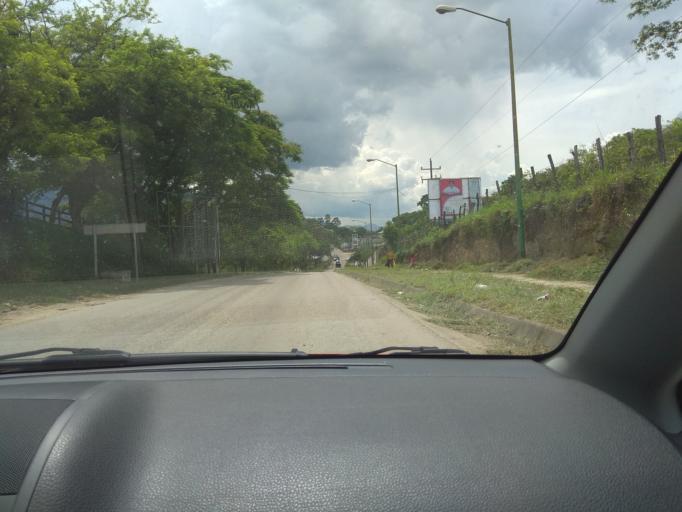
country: MX
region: Chiapas
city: Ocosingo
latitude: 16.8971
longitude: -92.0751
